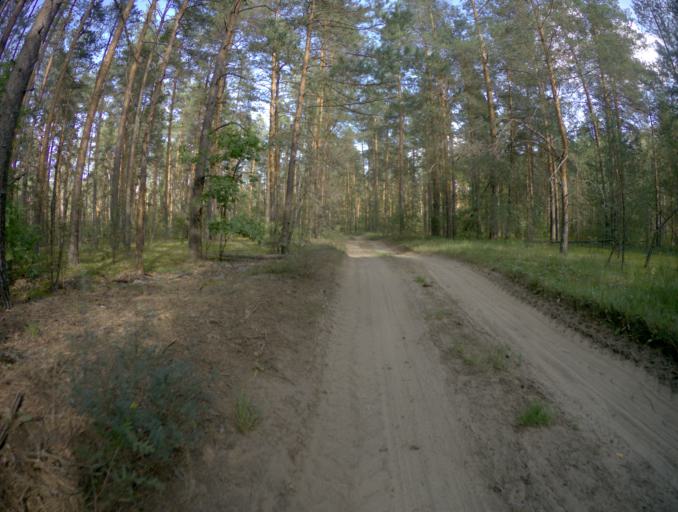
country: RU
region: Vladimir
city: Petushki
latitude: 55.8851
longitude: 39.4695
